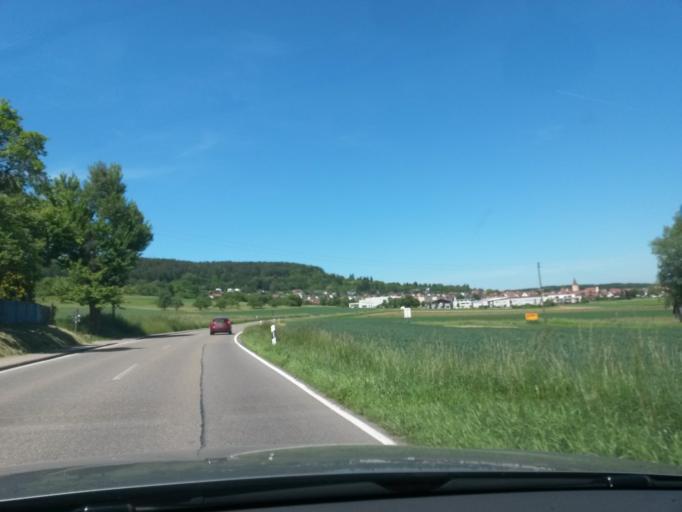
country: DE
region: Baden-Wuerttemberg
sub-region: Regierungsbezirk Stuttgart
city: Weil der Stadt
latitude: 48.7583
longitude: 8.8615
